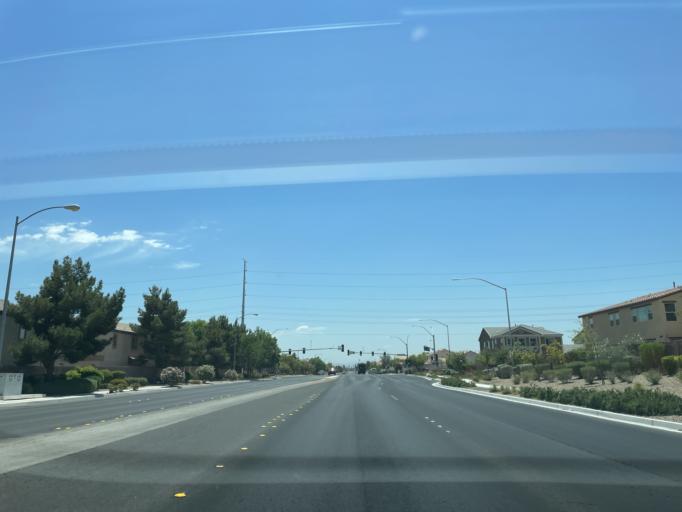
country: US
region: Nevada
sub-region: Clark County
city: North Las Vegas
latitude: 36.2780
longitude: -115.1532
